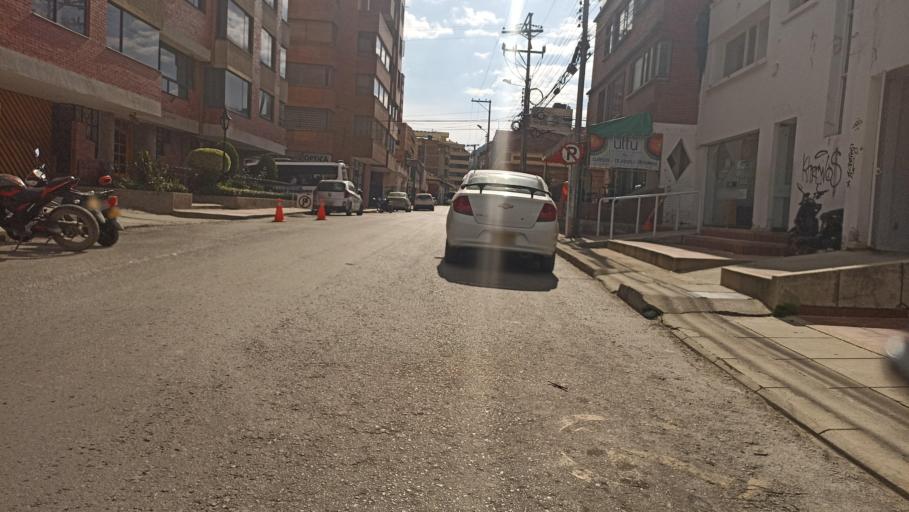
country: CO
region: Boyaca
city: Duitama
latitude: 5.8301
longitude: -73.0324
